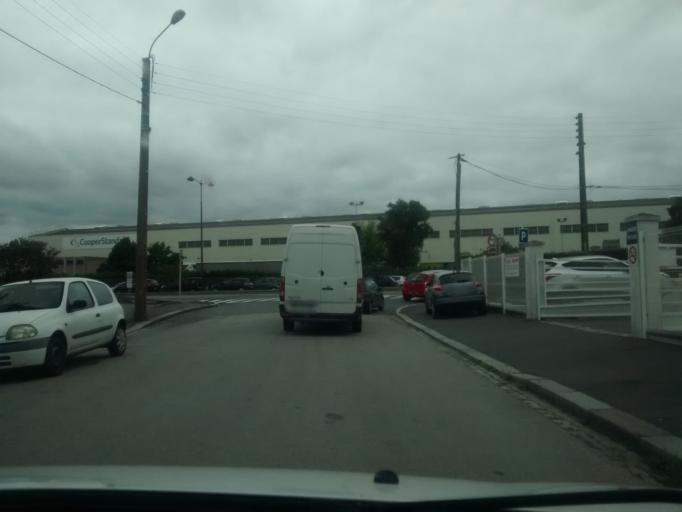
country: FR
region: Brittany
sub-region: Departement d'Ille-et-Vilaine
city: Vezin-le-Coquet
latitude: 48.1067
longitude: -1.7204
